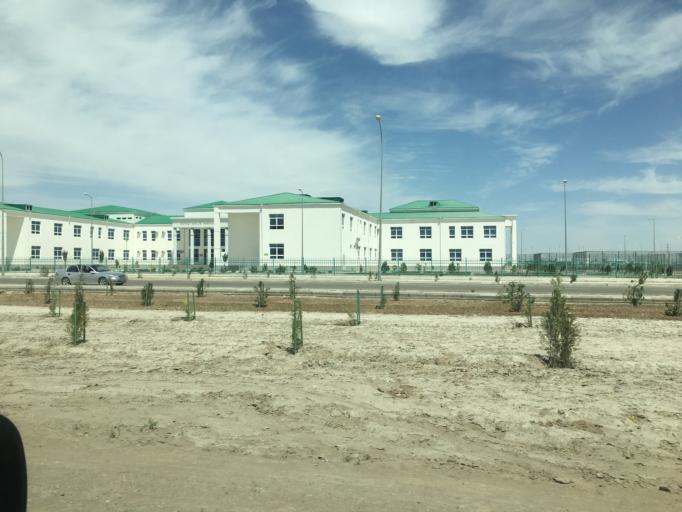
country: TM
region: Dasoguz
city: Dasoguz
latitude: 41.8132
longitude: 59.9518
